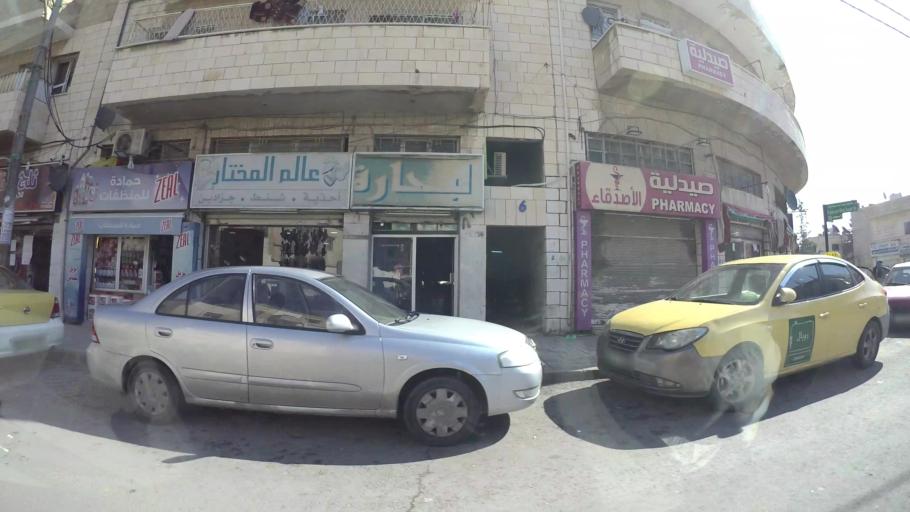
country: JO
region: Amman
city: Amman
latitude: 31.9879
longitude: 35.9896
